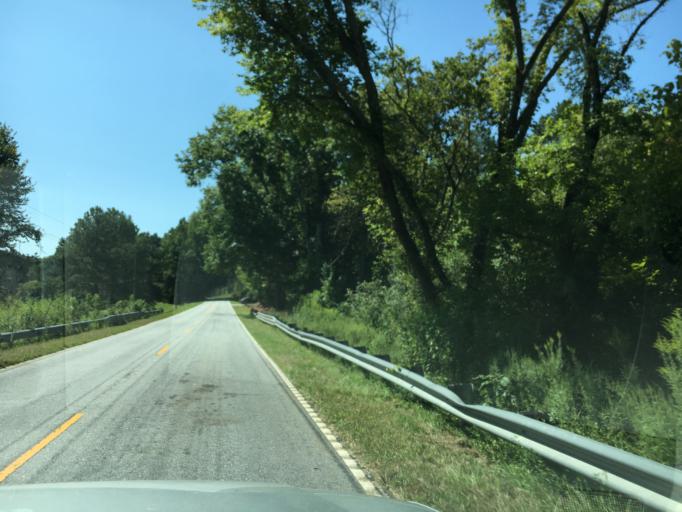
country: US
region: South Carolina
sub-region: Laurens County
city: Clinton
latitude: 34.4235
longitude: -81.8683
